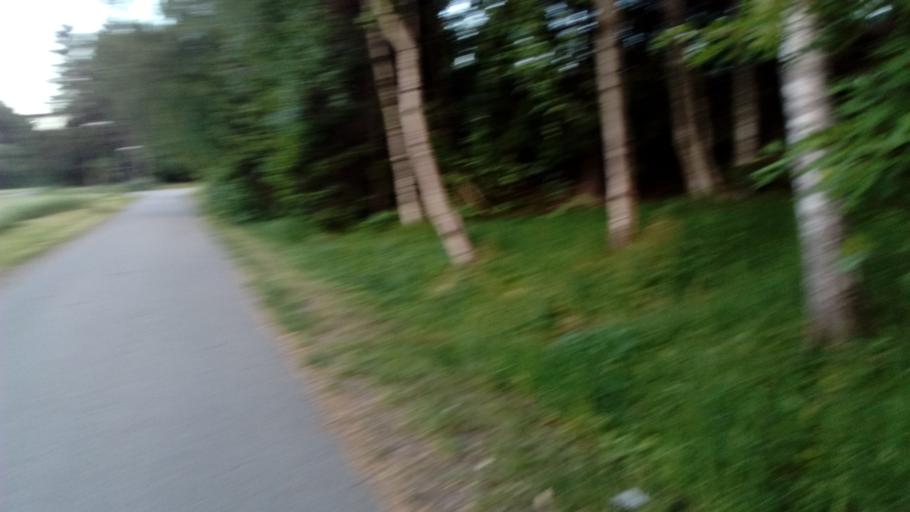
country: SE
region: Stockholm
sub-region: Tyreso Kommun
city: Bollmora
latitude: 59.2438
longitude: 18.2458
